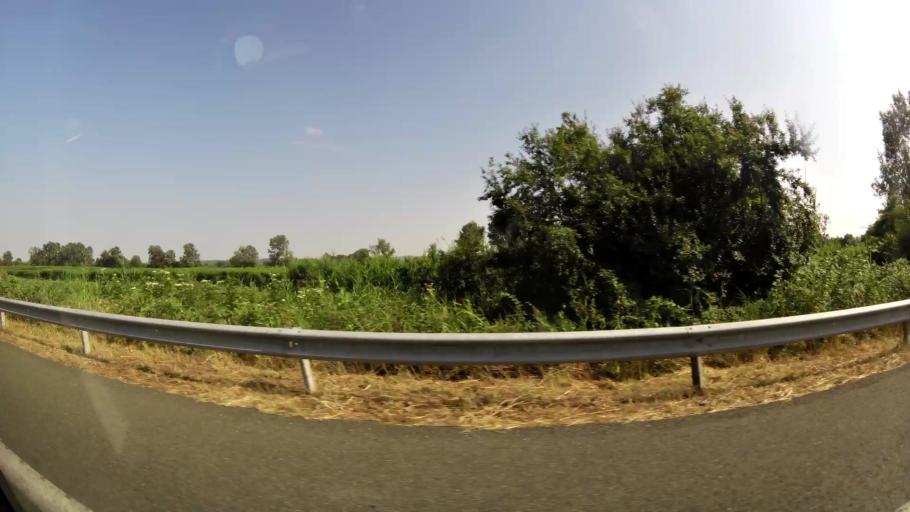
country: GR
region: Central Macedonia
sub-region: Nomos Imathias
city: Loutros
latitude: 40.5872
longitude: 22.4309
